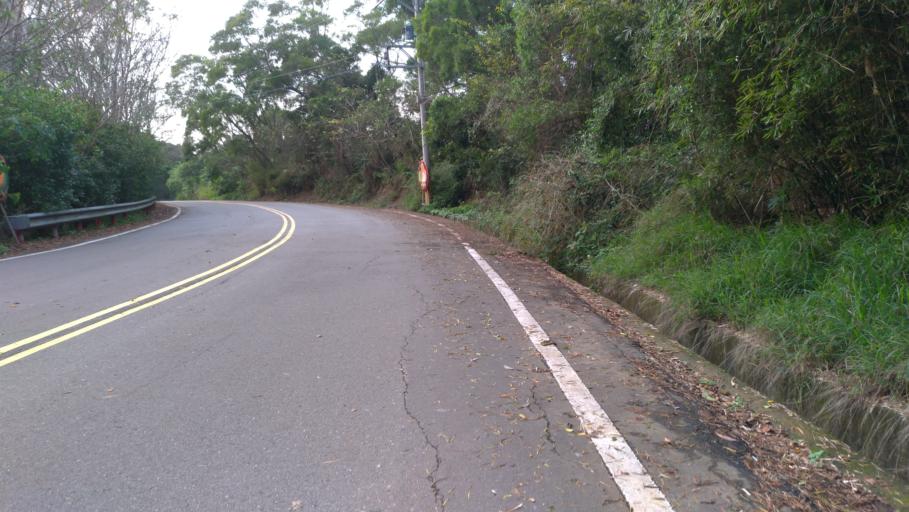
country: TW
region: Taiwan
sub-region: Hsinchu
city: Hsinchu
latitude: 24.7542
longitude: 120.9904
